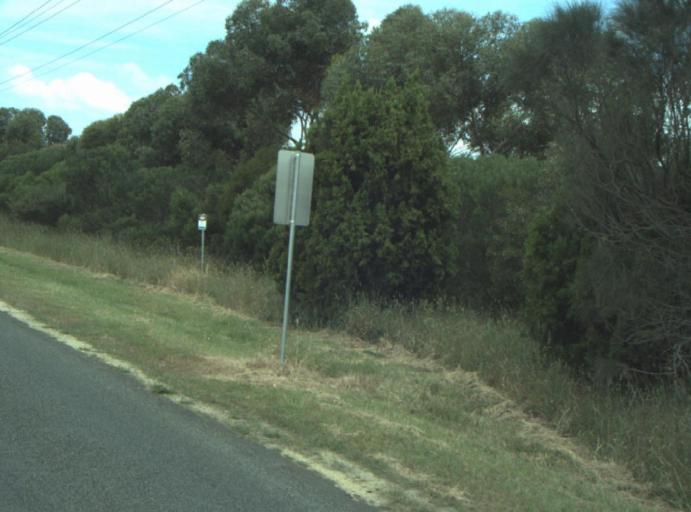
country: AU
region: Victoria
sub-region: Greater Geelong
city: Wandana Heights
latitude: -38.2218
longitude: 144.2999
